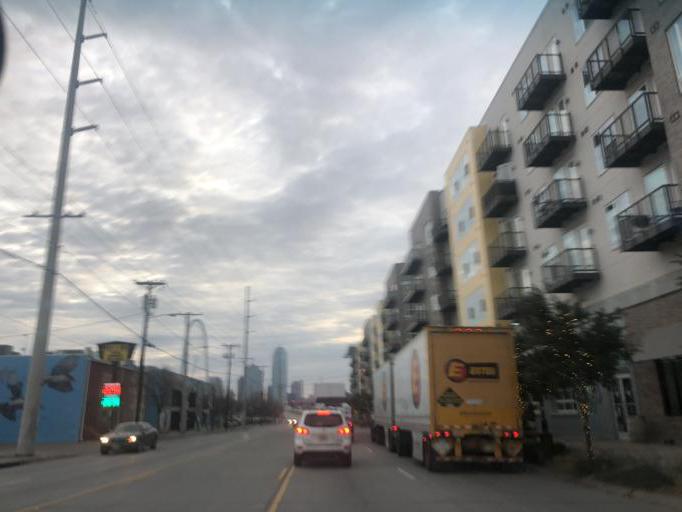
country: US
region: Texas
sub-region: Dallas County
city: Dallas
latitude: 32.7786
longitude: -96.8302
